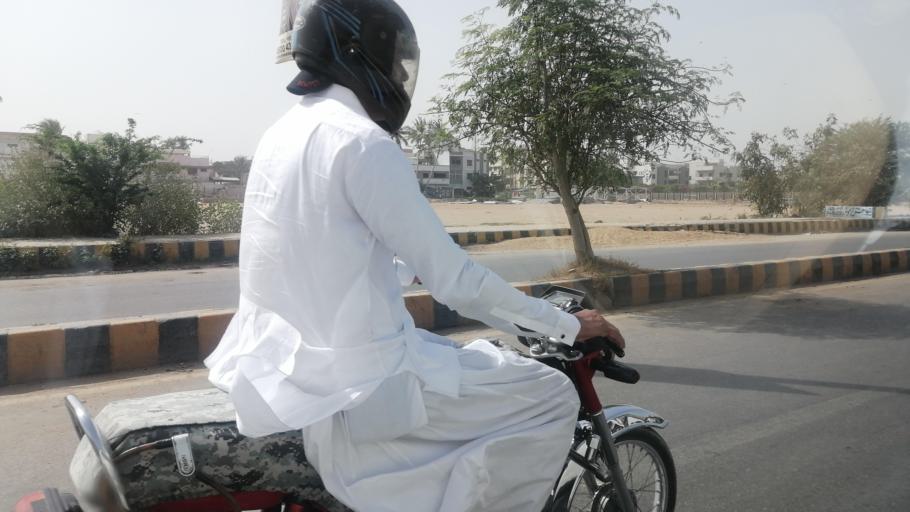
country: PK
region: Sindh
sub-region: Karachi District
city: Karachi
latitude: 24.9100
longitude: 67.0862
